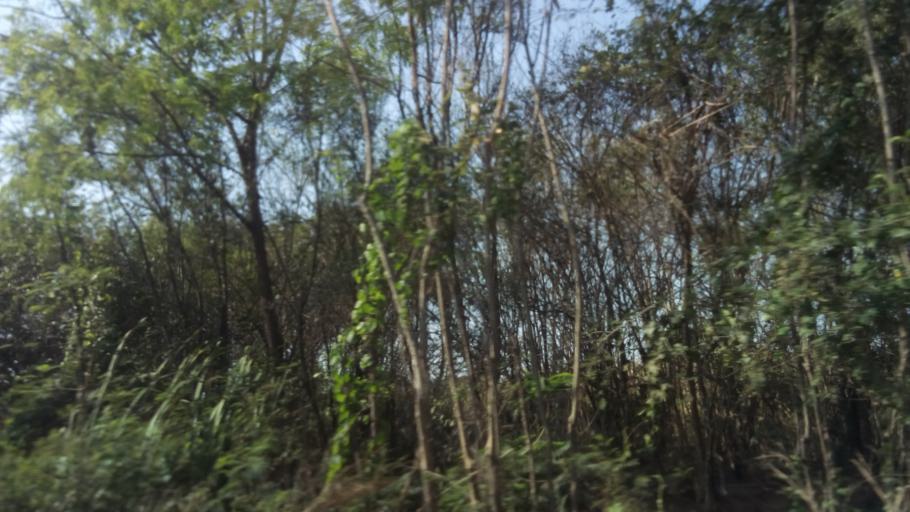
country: TH
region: Nonthaburi
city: Bang Yai
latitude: 13.8818
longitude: 100.3221
